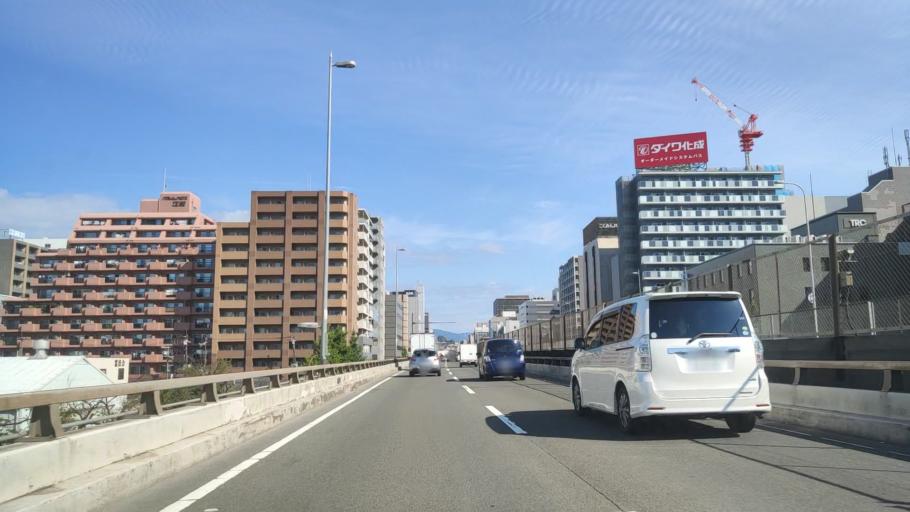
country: JP
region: Osaka
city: Suita
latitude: 34.7535
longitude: 135.4966
